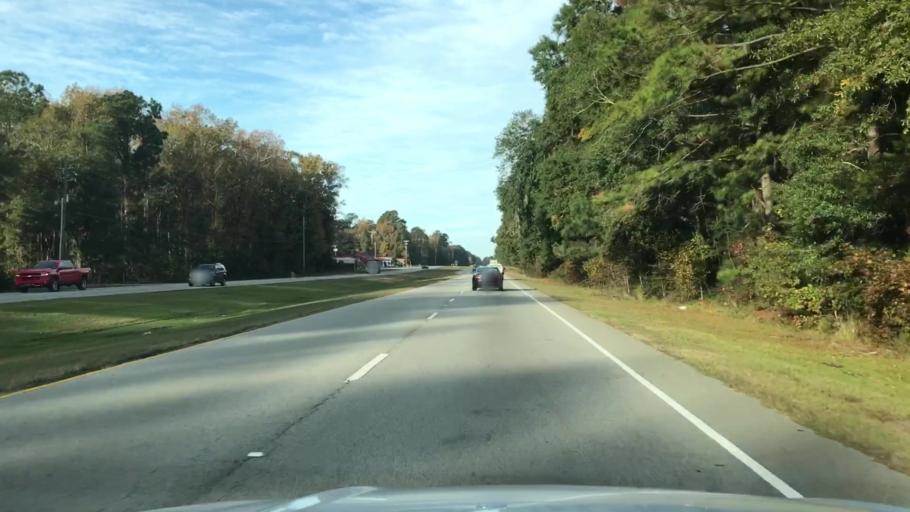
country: US
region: South Carolina
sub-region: Charleston County
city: Ravenel
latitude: 32.7808
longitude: -80.1847
